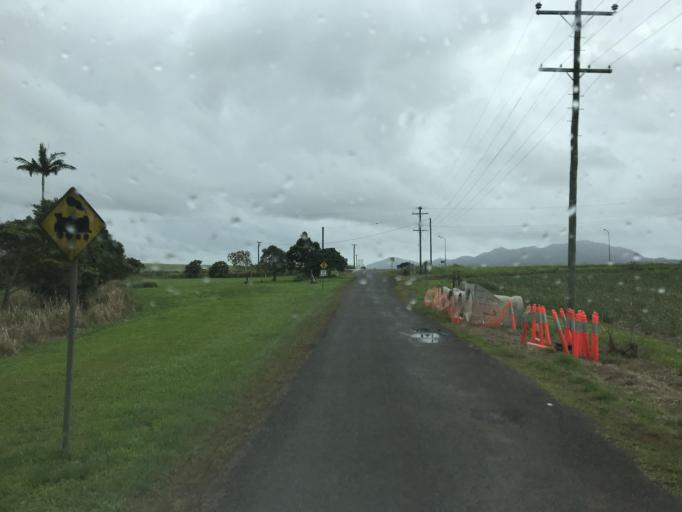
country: AU
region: Queensland
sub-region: Cassowary Coast
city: Innisfail
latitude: -17.4820
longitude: 145.9894
